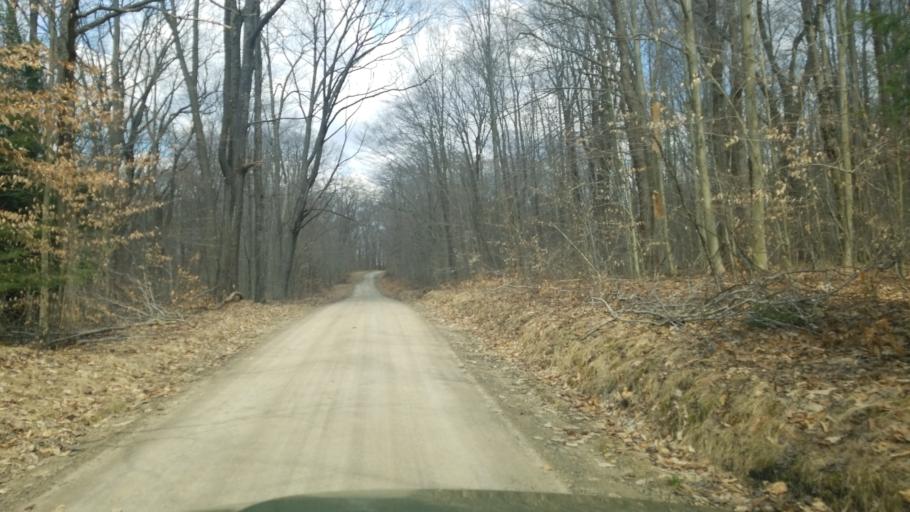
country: US
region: Pennsylvania
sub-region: Clearfield County
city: Clearfield
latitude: 41.1538
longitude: -78.5172
